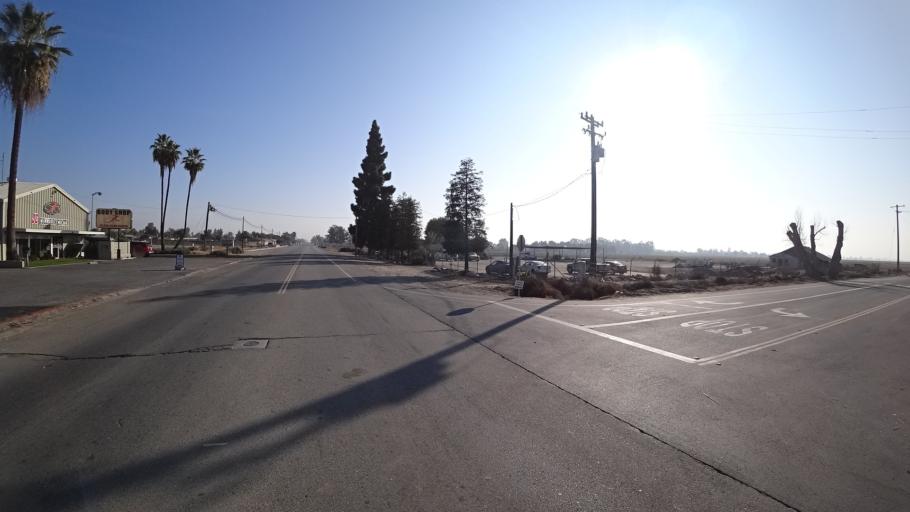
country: US
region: California
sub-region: Kern County
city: Greenfield
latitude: 35.2668
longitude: -119.0121
